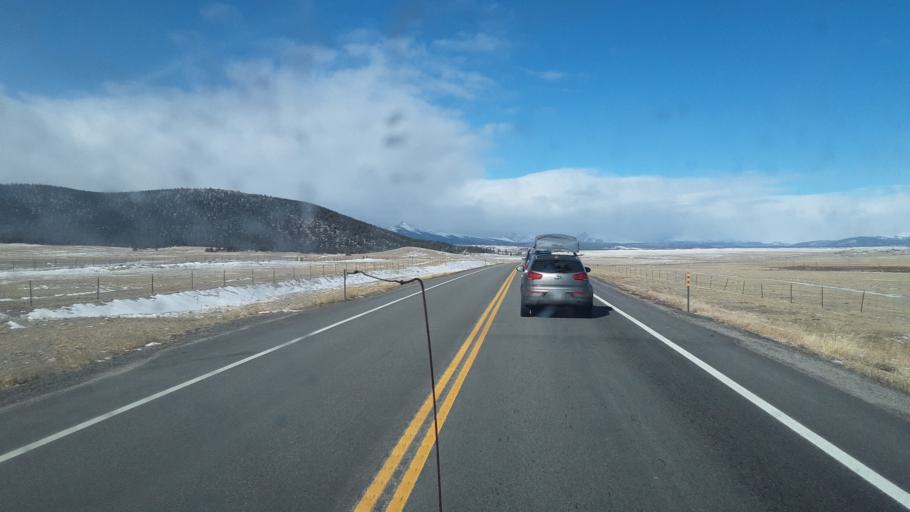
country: US
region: Colorado
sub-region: Park County
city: Fairplay
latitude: 39.0891
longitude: -105.9824
